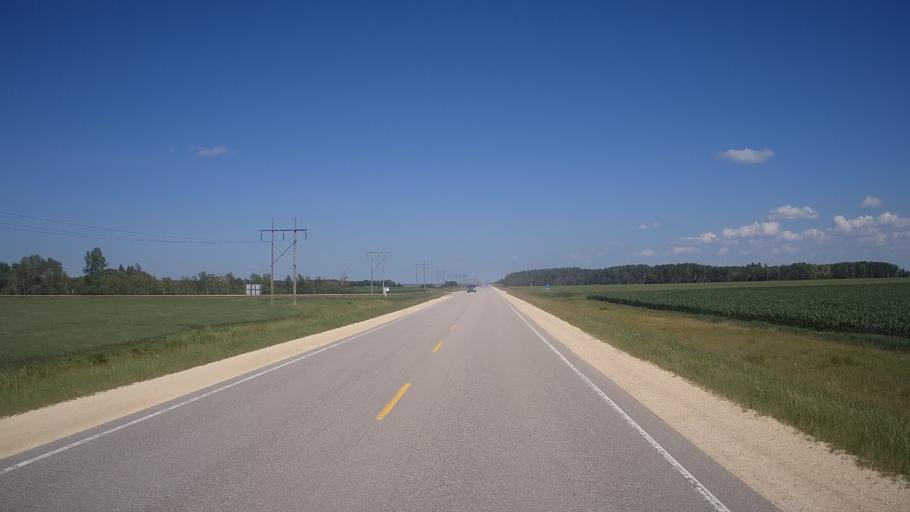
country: CA
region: Manitoba
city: Stonewall
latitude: 50.1227
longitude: -97.4626
